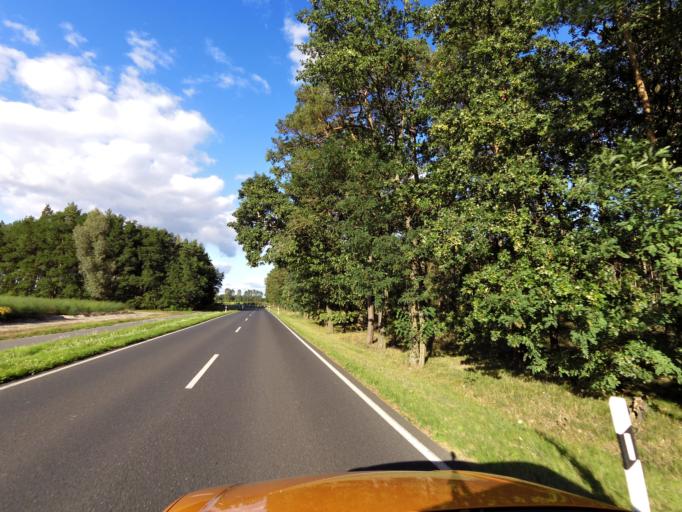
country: DE
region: Brandenburg
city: Luckenwalde
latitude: 52.1446
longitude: 13.1849
